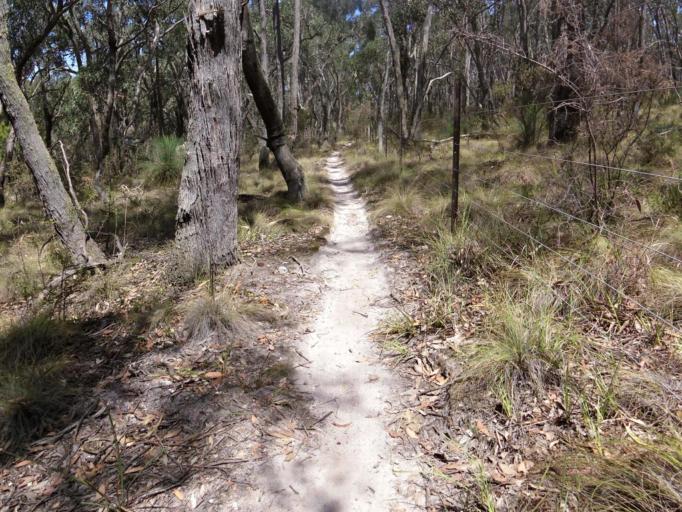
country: AU
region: Victoria
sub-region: Melton
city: Melton West
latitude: -37.5120
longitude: 144.5553
